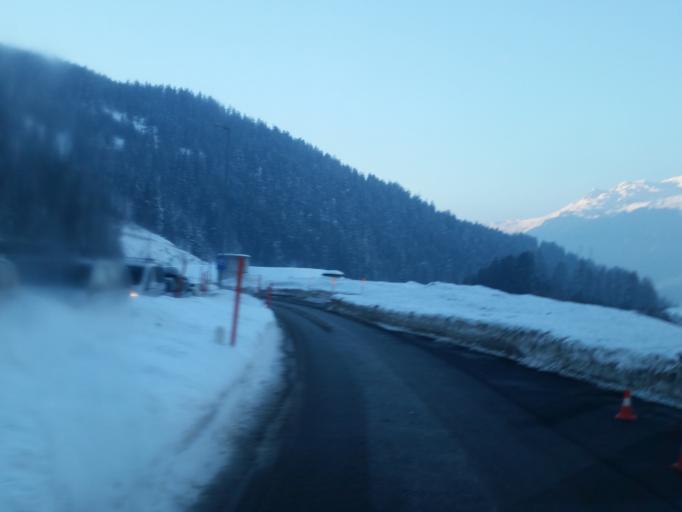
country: CH
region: Grisons
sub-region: Praettigau/Davos District
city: Klosters Serneus
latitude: 46.8563
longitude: 9.8839
